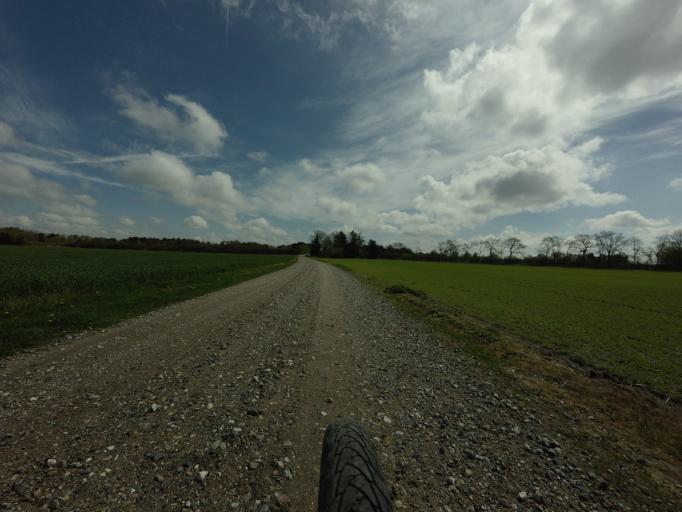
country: DK
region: North Denmark
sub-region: Jammerbugt Kommune
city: Kas
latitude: 57.1987
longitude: 9.6208
